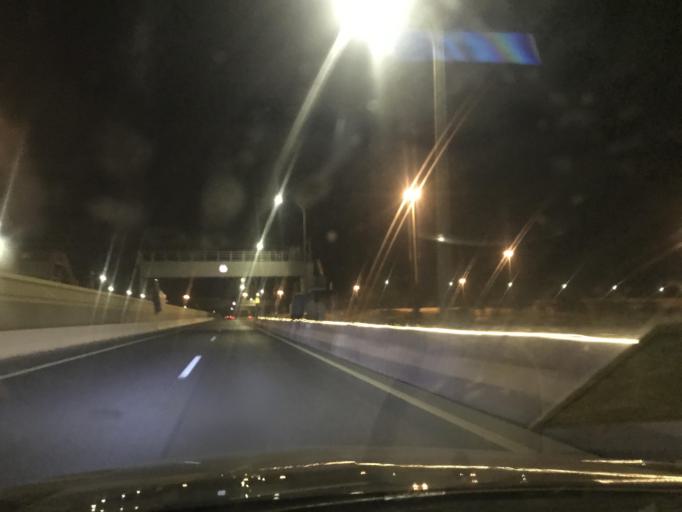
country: SA
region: Ar Riyad
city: Riyadh
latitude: 24.9045
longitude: 46.7099
